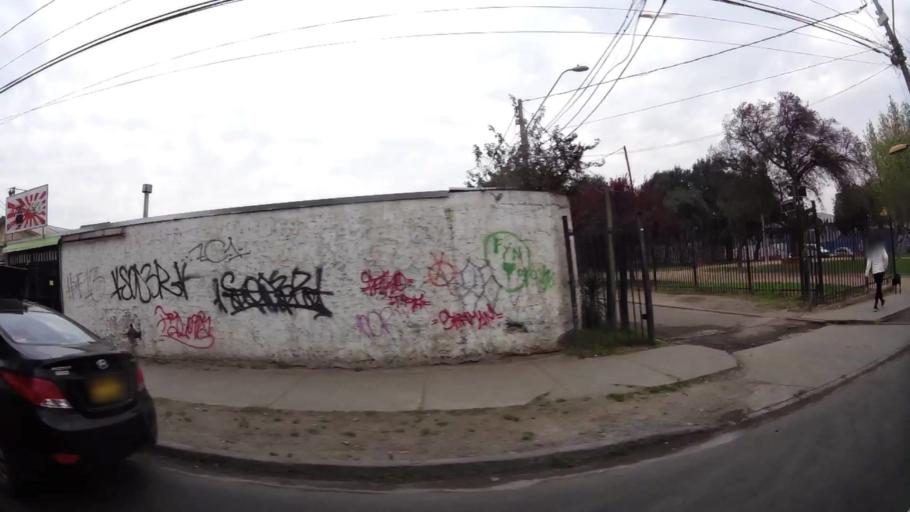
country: CL
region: Santiago Metropolitan
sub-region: Provincia de Santiago
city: Lo Prado
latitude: -33.4943
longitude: -70.7363
